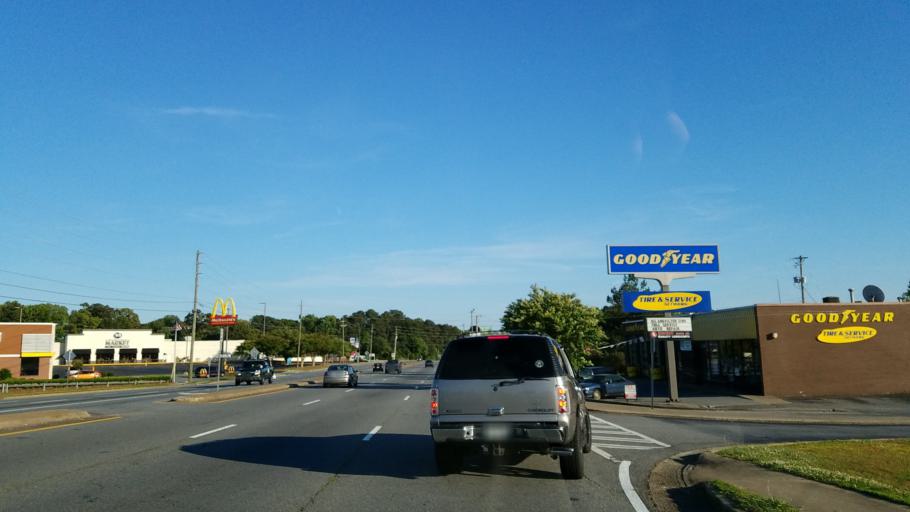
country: US
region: Georgia
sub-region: Cherokee County
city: Woodstock
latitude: 34.0870
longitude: -84.5768
